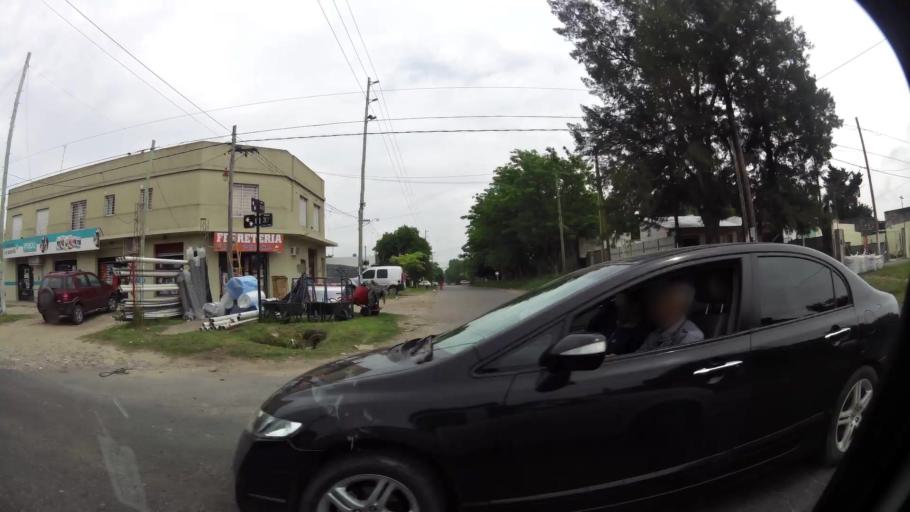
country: AR
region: Buenos Aires
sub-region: Partido de La Plata
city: La Plata
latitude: -34.9319
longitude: -58.0032
